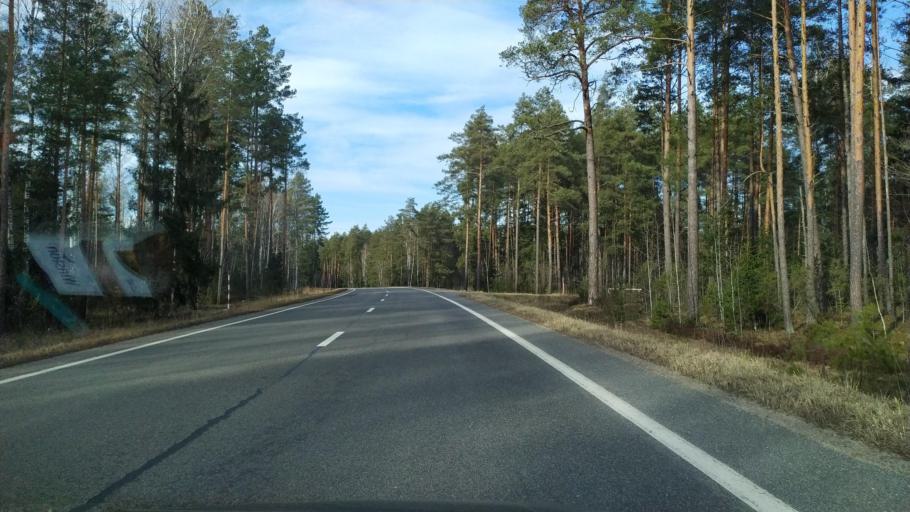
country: BY
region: Brest
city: Pruzhany
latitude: 52.5195
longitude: 24.1783
